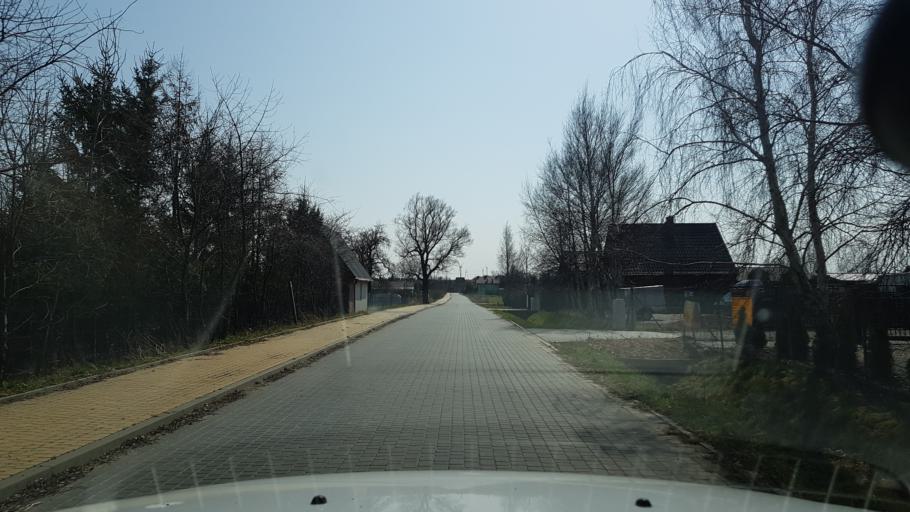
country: PL
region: West Pomeranian Voivodeship
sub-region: Powiat slawienski
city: Darlowo
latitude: 54.5124
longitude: 16.4996
